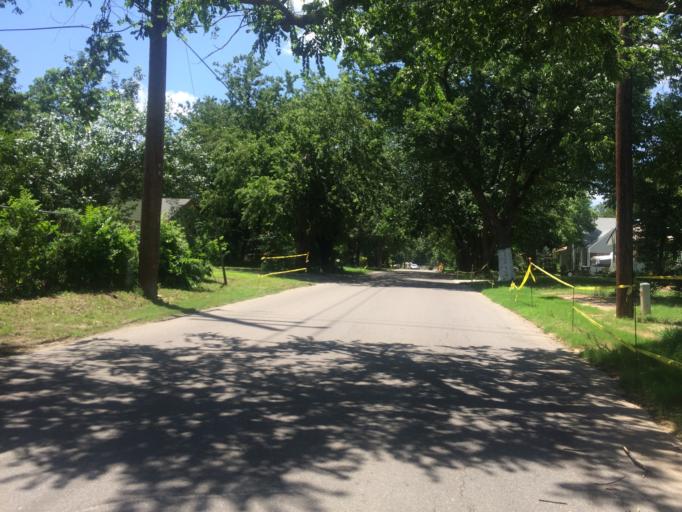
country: US
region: Oklahoma
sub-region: Cleveland County
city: Norman
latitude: 35.2148
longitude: -97.4551
